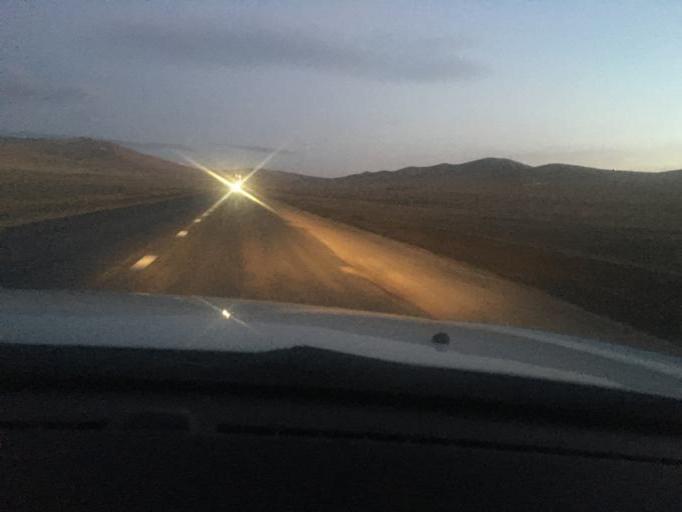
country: MN
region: Central Aimak
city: Altanbulag
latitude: 47.9873
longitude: 106.5627
